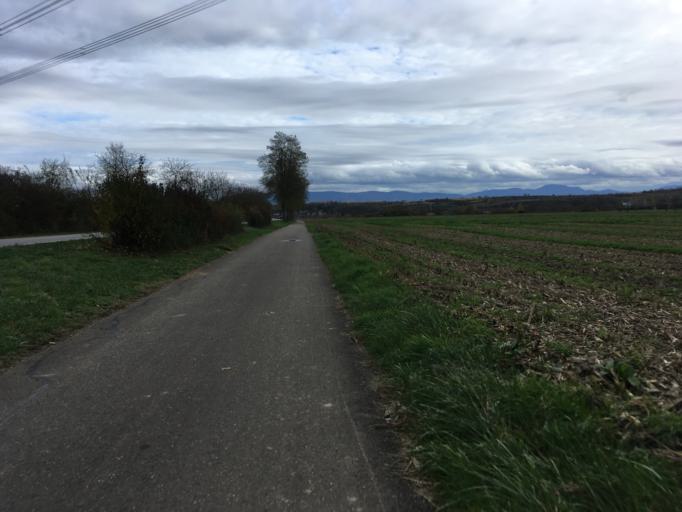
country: DE
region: Baden-Wuerttemberg
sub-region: Freiburg Region
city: Merdingen
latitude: 48.0264
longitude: 7.6662
